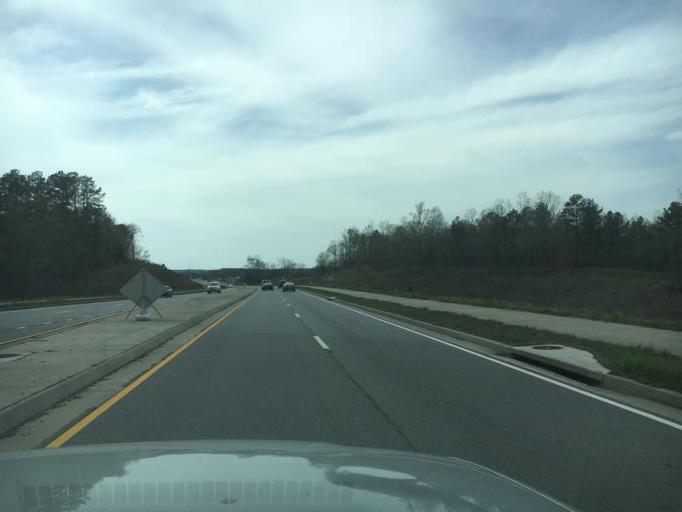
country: US
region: Georgia
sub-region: Hall County
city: Flowery Branch
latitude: 34.1100
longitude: -83.8654
